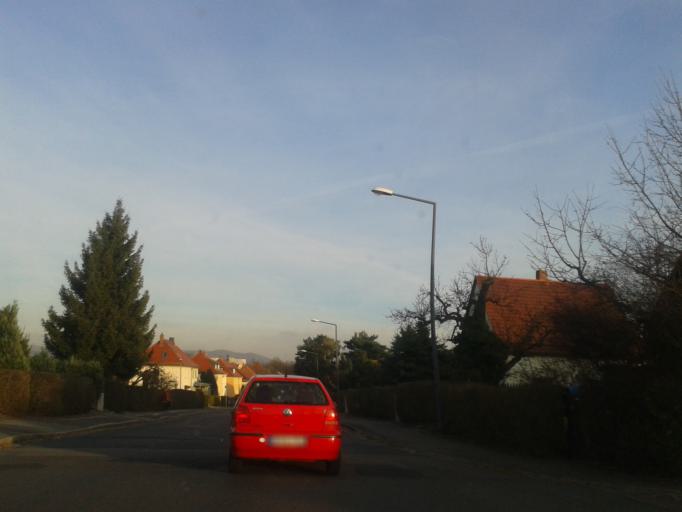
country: DE
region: Saxony
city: Heidenau
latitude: 50.9978
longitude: 13.8109
